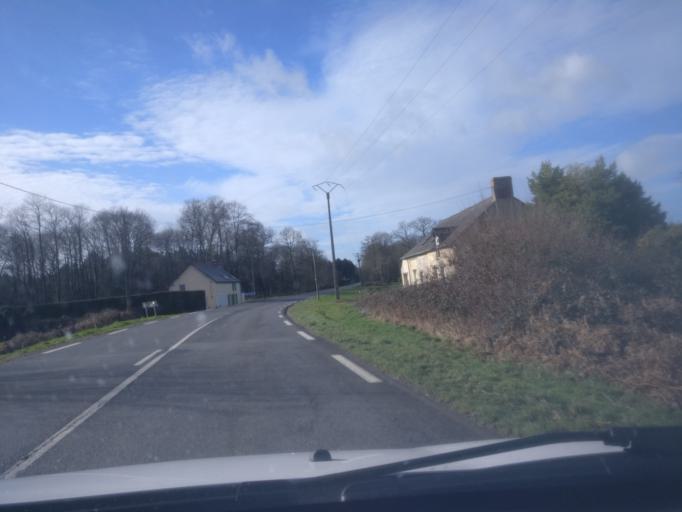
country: FR
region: Brittany
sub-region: Departement d'Ille-et-Vilaine
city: Sens-de-Bretagne
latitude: 48.2977
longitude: -1.5571
